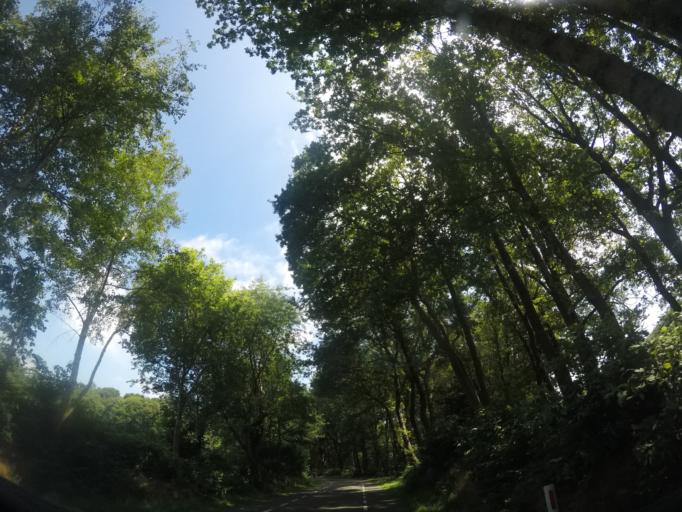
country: NL
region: Overijssel
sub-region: Gemeente Dalfsen
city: Dalfsen
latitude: 52.4920
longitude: 6.2533
